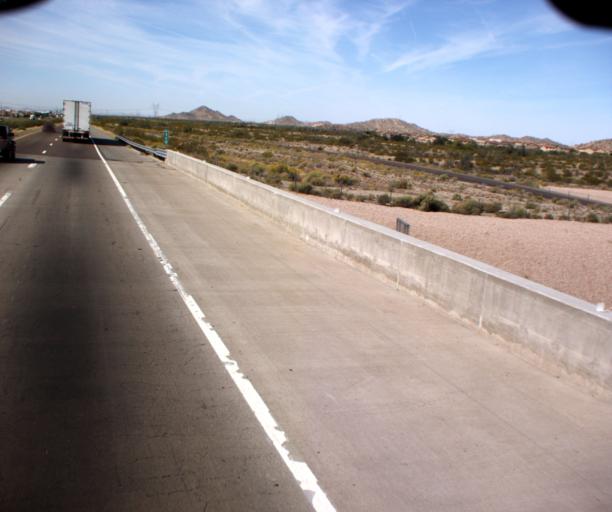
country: US
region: Arizona
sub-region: Maricopa County
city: Buckeye
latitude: 33.4449
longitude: -112.5563
